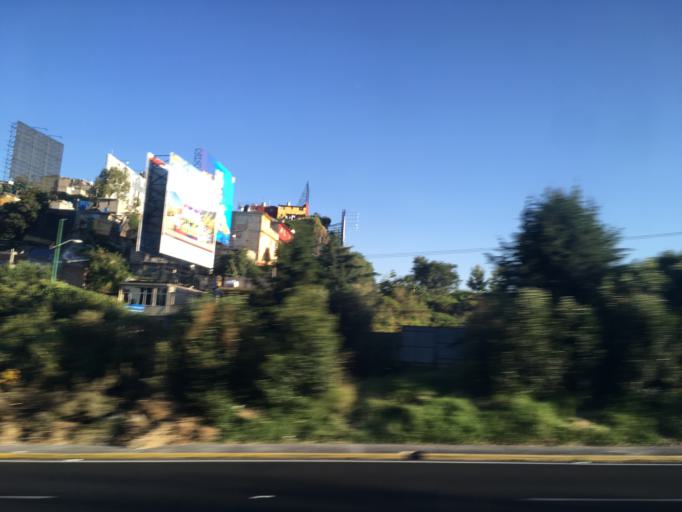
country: MX
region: Mexico City
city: Col. Bosques de las Lomas
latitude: 19.3797
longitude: -99.2524
